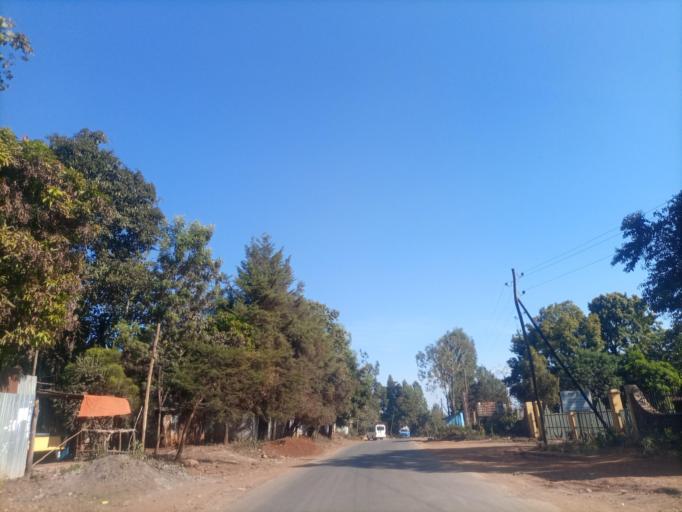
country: ET
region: Oromiya
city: Jima
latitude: 7.6989
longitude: 36.8143
